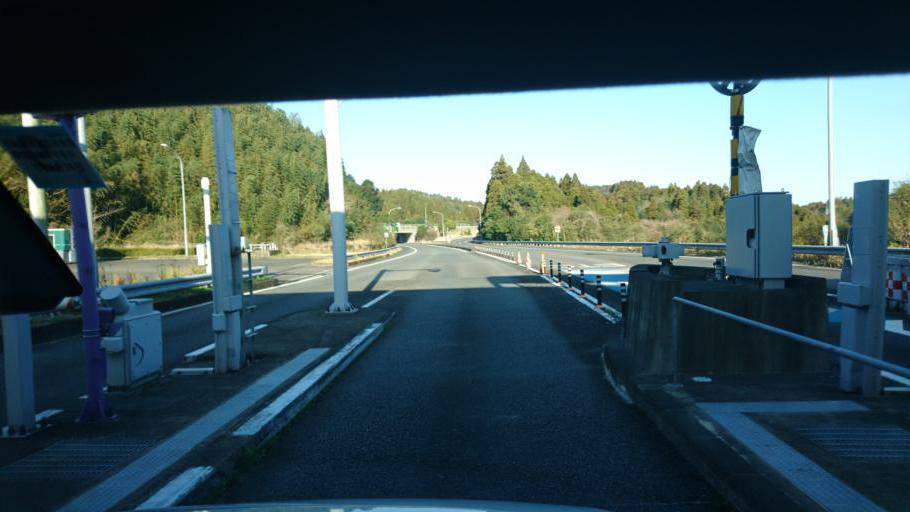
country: JP
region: Miyazaki
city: Miyazaki-shi
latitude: 31.8675
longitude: 131.3616
